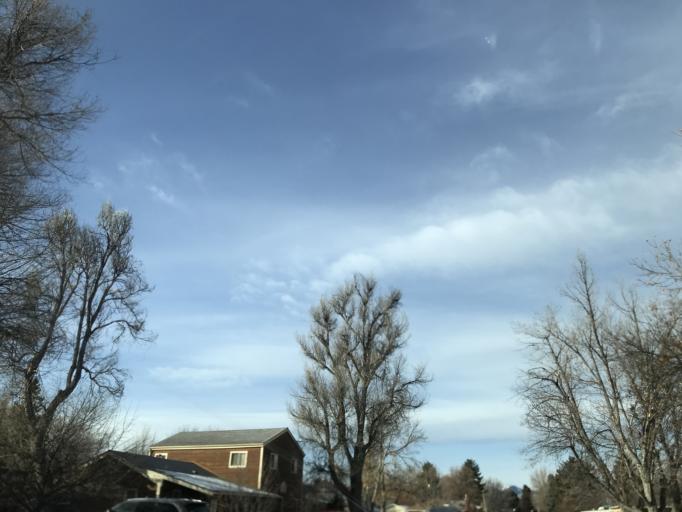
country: US
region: Colorado
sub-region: Arapahoe County
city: Littleton
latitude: 39.6042
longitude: -105.0128
